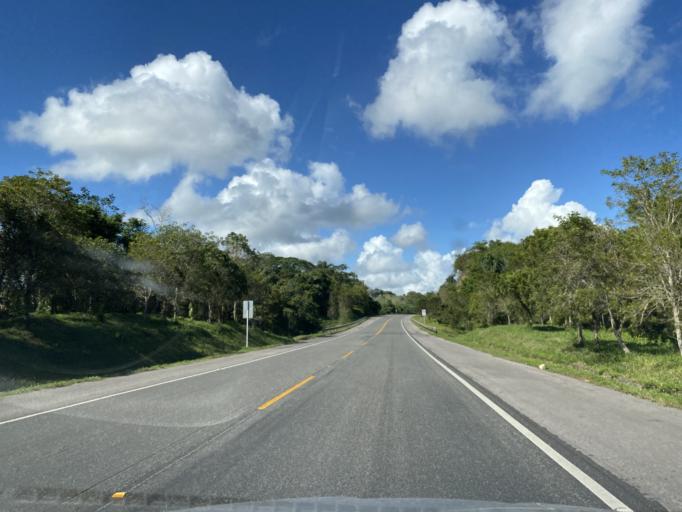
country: DO
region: Monte Plata
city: Majagual
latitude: 19.0305
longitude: -69.8253
